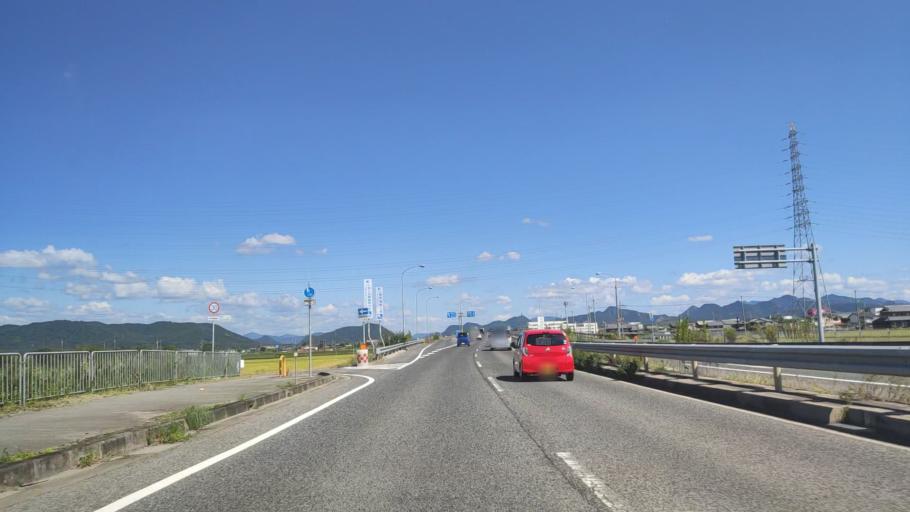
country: JP
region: Hyogo
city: Yashiro
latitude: 34.9082
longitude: 134.9532
